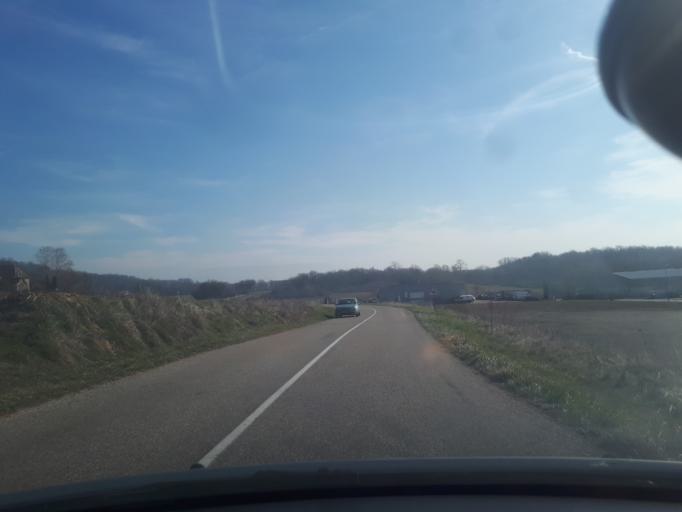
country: FR
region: Rhone-Alpes
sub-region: Departement de l'Isere
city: Sermerieu
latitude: 45.6684
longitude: 5.4189
